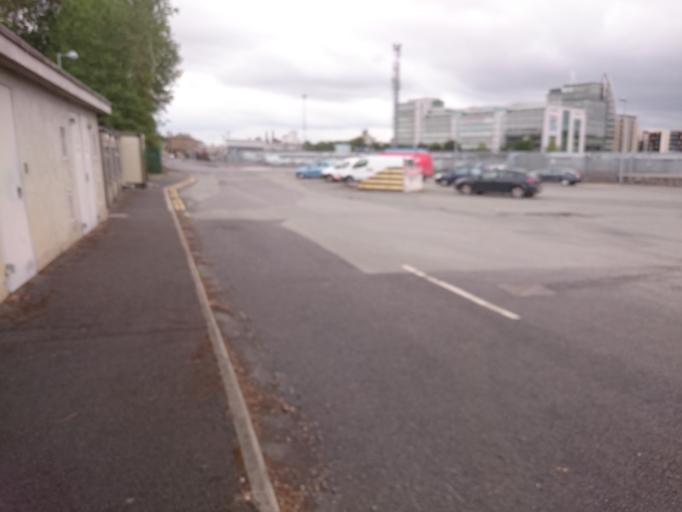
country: IE
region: Leinster
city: Rialto
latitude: 53.3473
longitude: -6.3008
